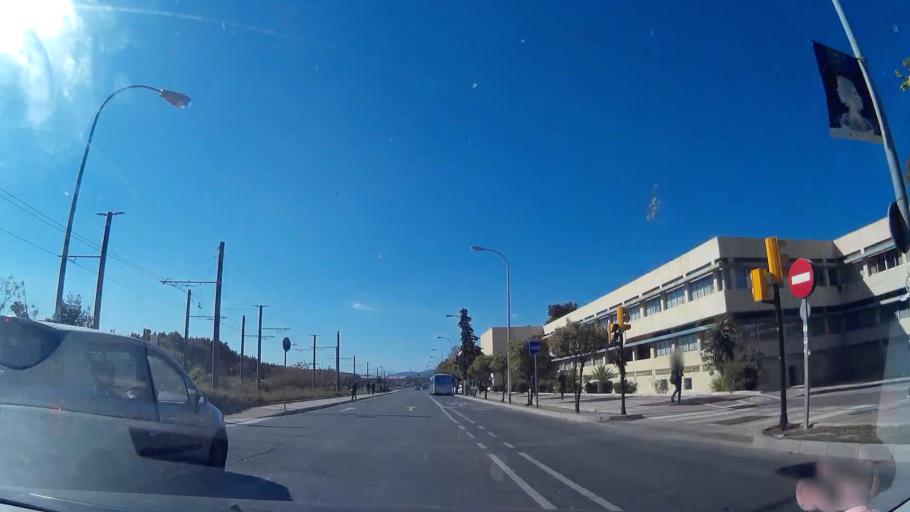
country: ES
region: Andalusia
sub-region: Provincia de Malaga
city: Malaga
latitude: 36.7171
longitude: -4.4726
